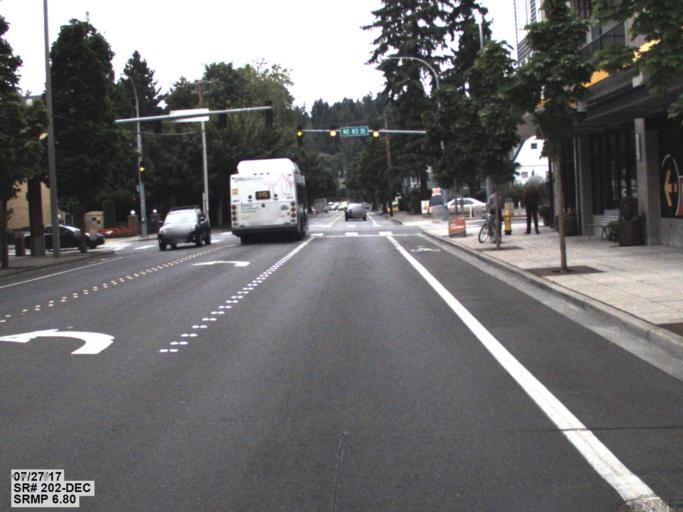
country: US
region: Washington
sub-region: King County
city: Redmond
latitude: 47.6763
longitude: -122.1216
